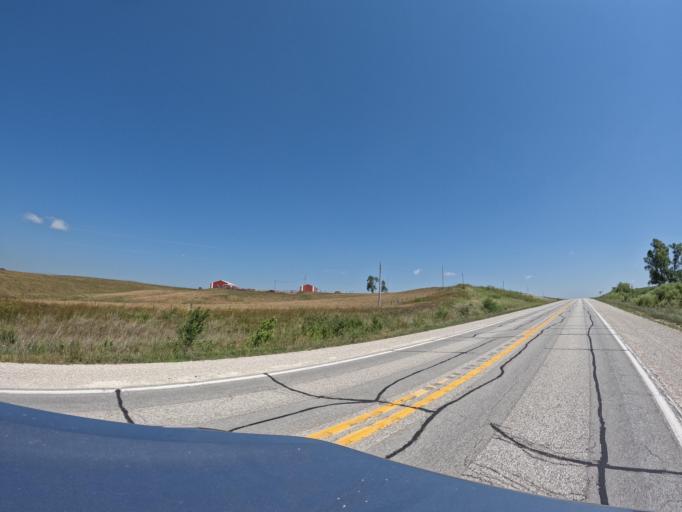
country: US
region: Iowa
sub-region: Keokuk County
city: Sigourney
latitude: 41.2432
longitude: -92.2096
